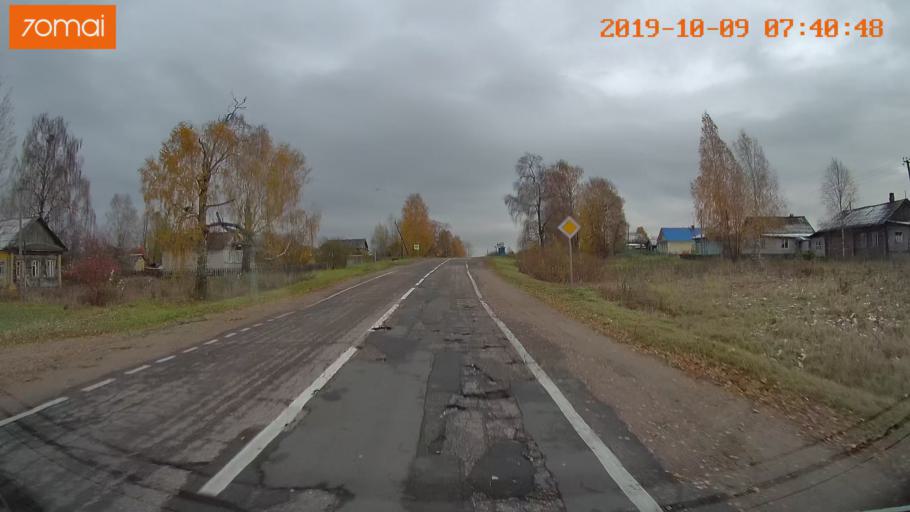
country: RU
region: Jaroslavl
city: Kukoboy
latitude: 58.6361
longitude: 39.6982
